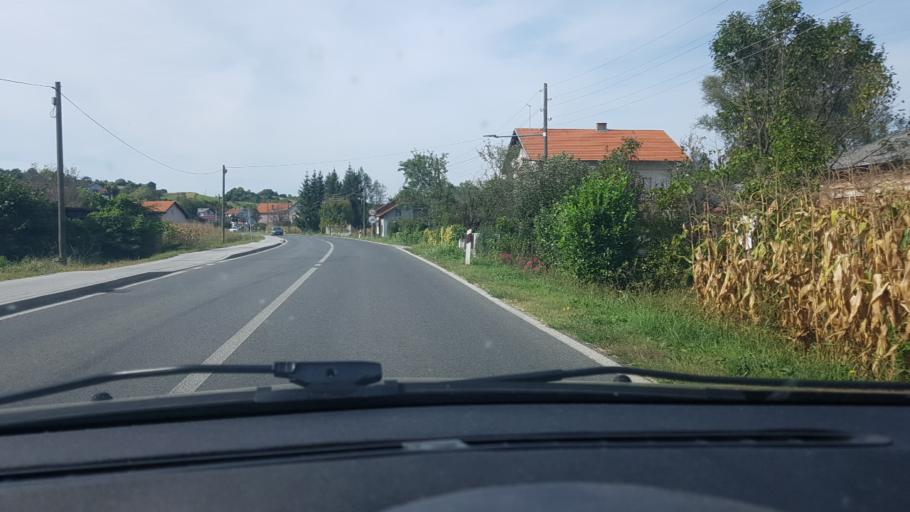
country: HR
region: Krapinsko-Zagorska
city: Zlatar
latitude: 46.1002
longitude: 16.0646
